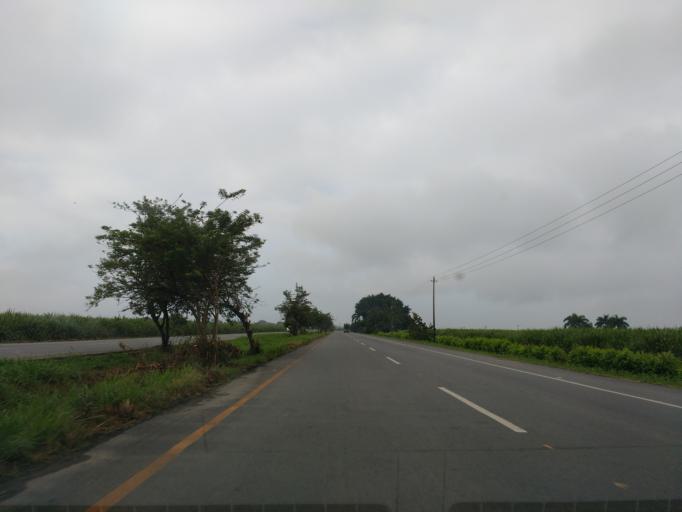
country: CO
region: Valle del Cauca
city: Palmira
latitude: 3.5420
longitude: -76.3384
